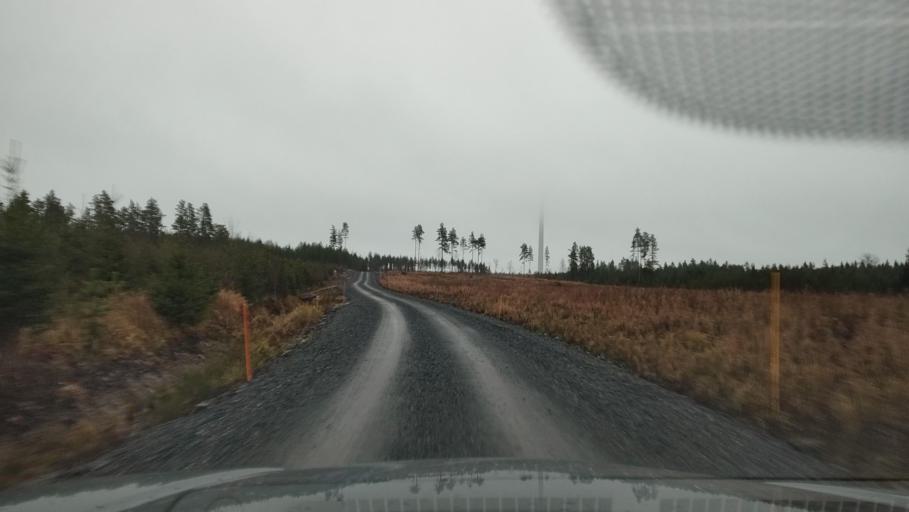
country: FI
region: Southern Ostrobothnia
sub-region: Suupohja
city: Karijoki
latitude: 62.1806
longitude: 21.5916
